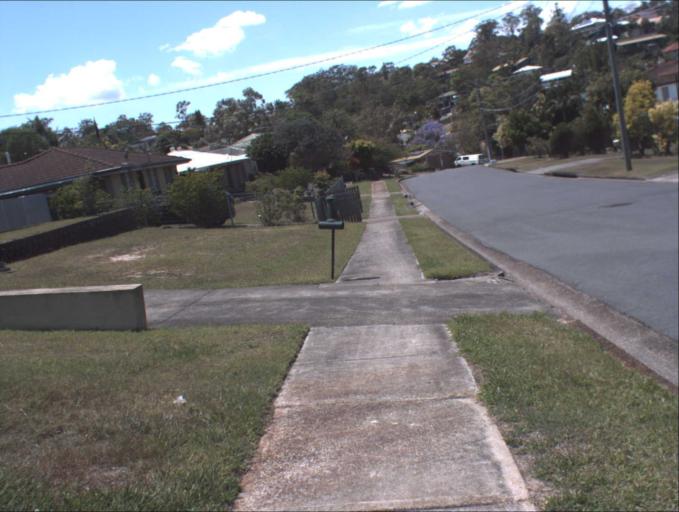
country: AU
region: Queensland
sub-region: Logan
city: Rochedale South
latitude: -27.6029
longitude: 153.1263
